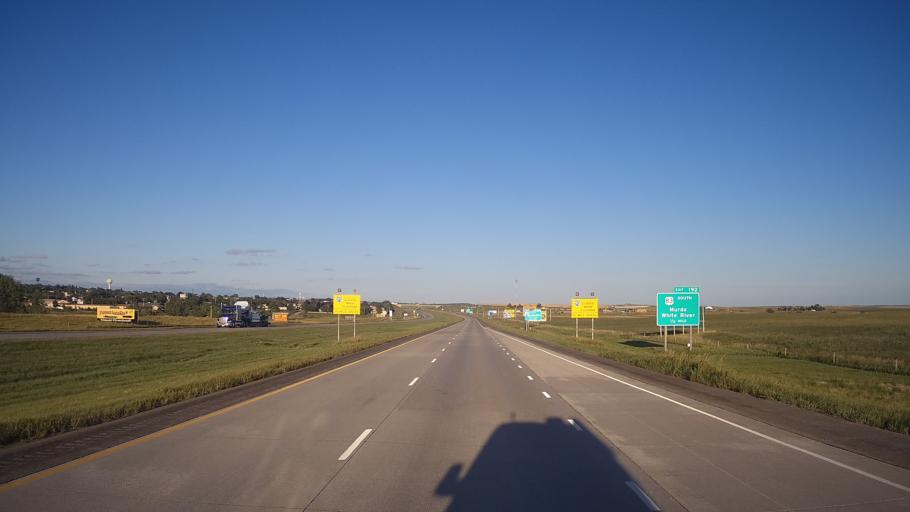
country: US
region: South Dakota
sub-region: Jones County
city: Murdo
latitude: 43.8840
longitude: -100.7254
